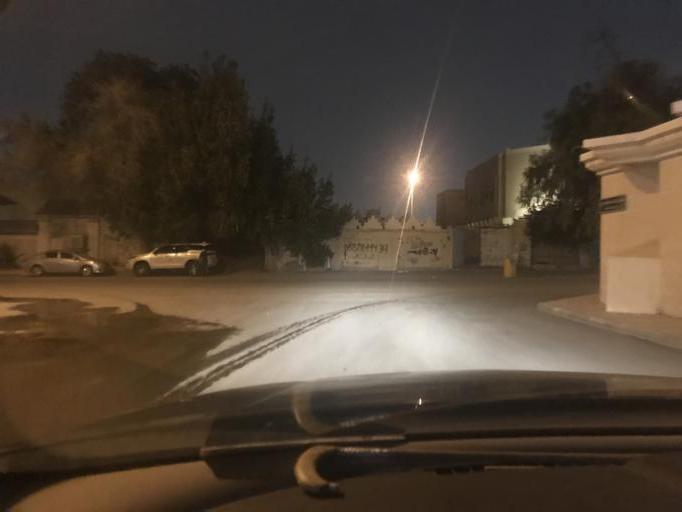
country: SA
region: Ar Riyad
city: Riyadh
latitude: 24.7490
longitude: 46.7756
